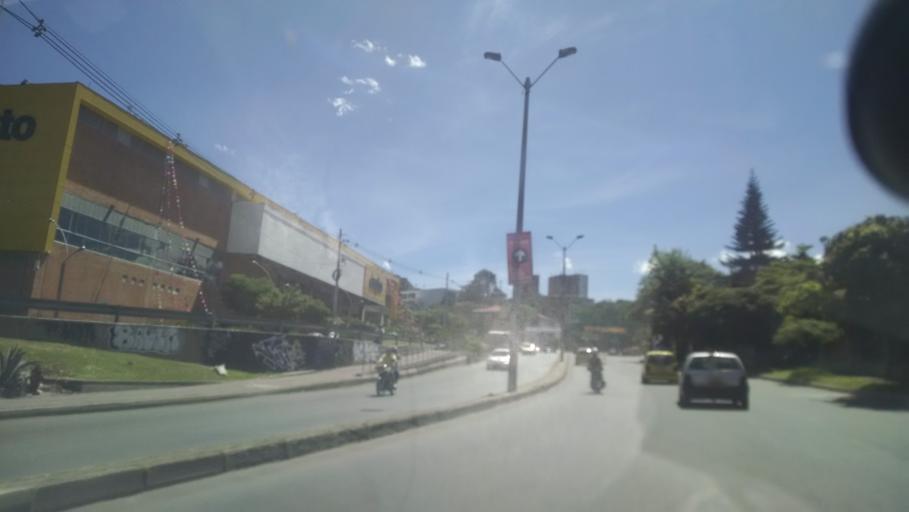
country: CO
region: Antioquia
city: Medellin
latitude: 6.2720
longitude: -75.5938
